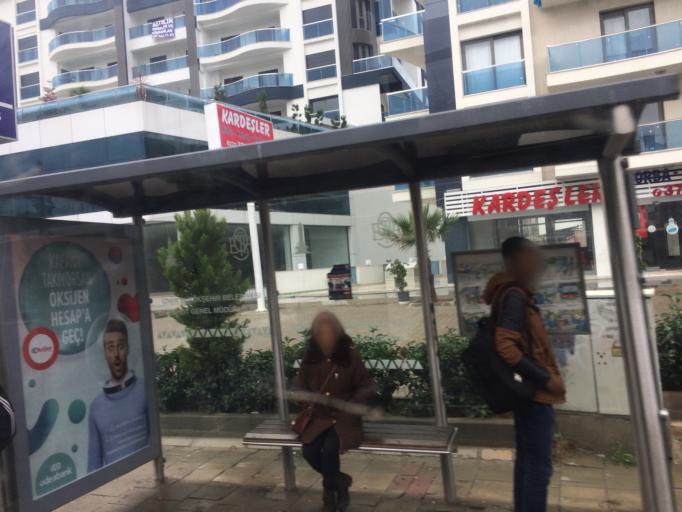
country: TR
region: Izmir
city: Karsiyaka
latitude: 38.5162
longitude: 27.0421
